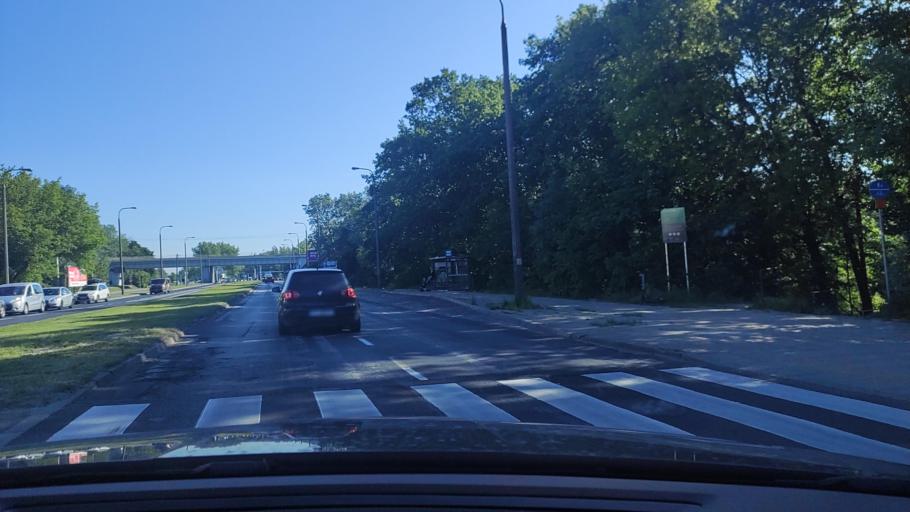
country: PL
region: Greater Poland Voivodeship
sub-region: Powiat poznanski
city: Lubon
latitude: 52.3692
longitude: 16.9153
